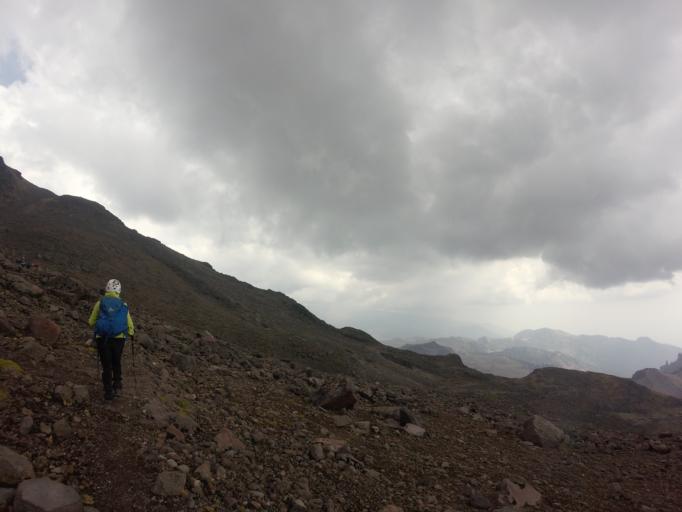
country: MX
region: Mexico
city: Amecameca de Juarez
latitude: 19.1569
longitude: -98.6430
